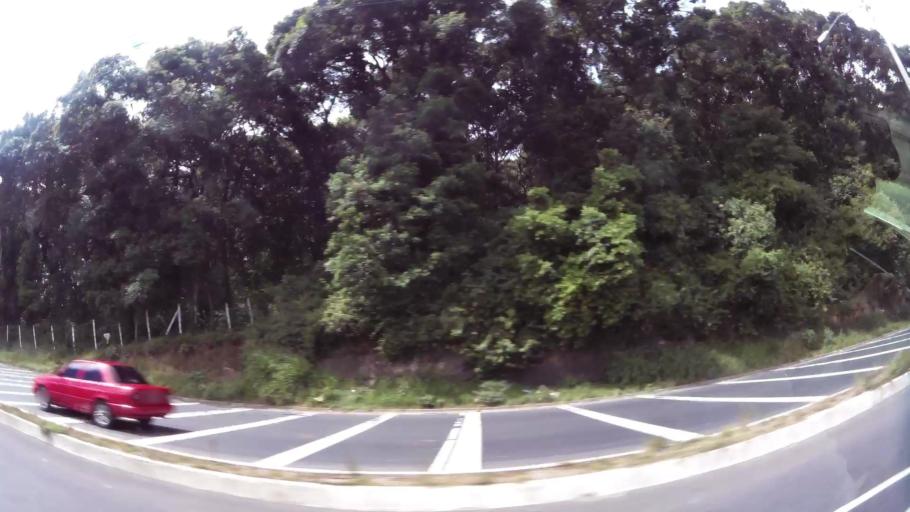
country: GT
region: Guatemala
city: Guatemala City
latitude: 14.6530
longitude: -90.5489
